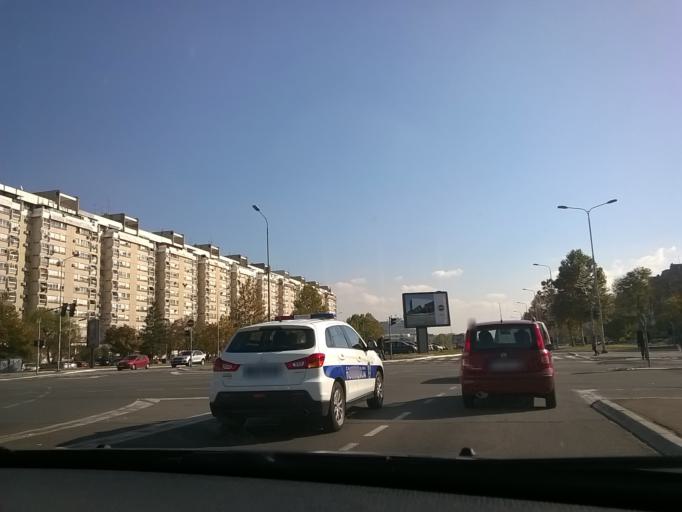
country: RS
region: Central Serbia
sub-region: Belgrade
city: Novi Beograd
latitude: 44.8192
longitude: 20.4144
